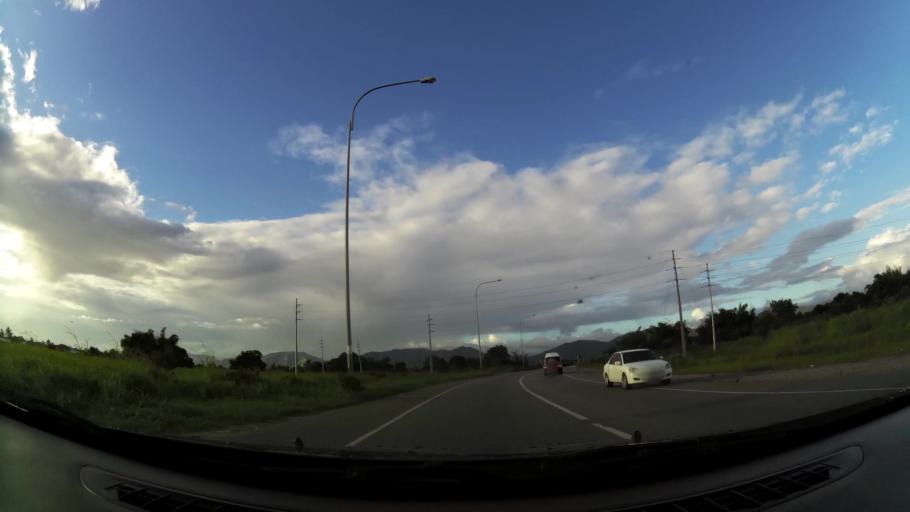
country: TT
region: Tunapuna/Piarco
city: Arouca
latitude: 10.5880
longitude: -61.3554
